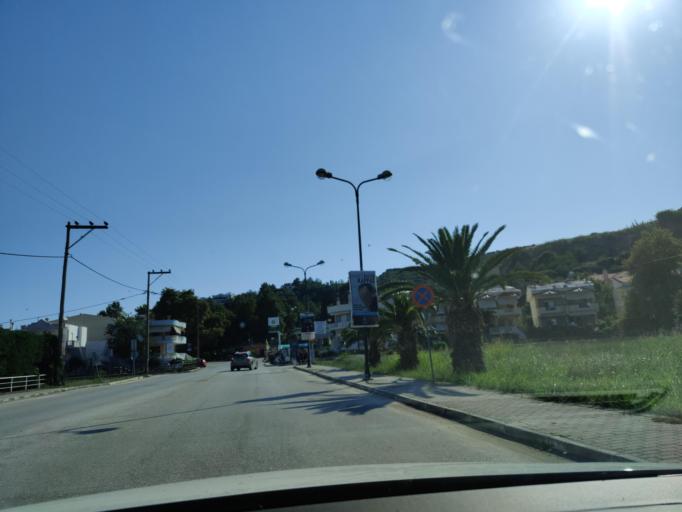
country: GR
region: East Macedonia and Thrace
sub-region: Nomos Kavalas
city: Nea Peramos
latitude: 40.8464
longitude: 24.3071
